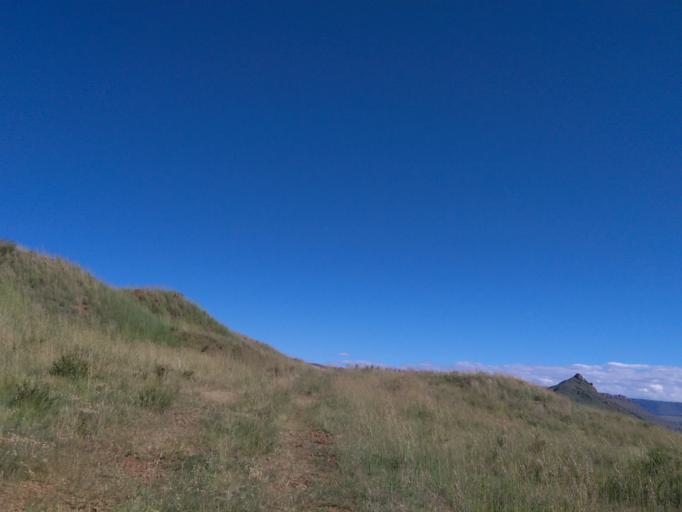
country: LS
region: Maseru
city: Maseru
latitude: -29.4840
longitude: 27.5815
